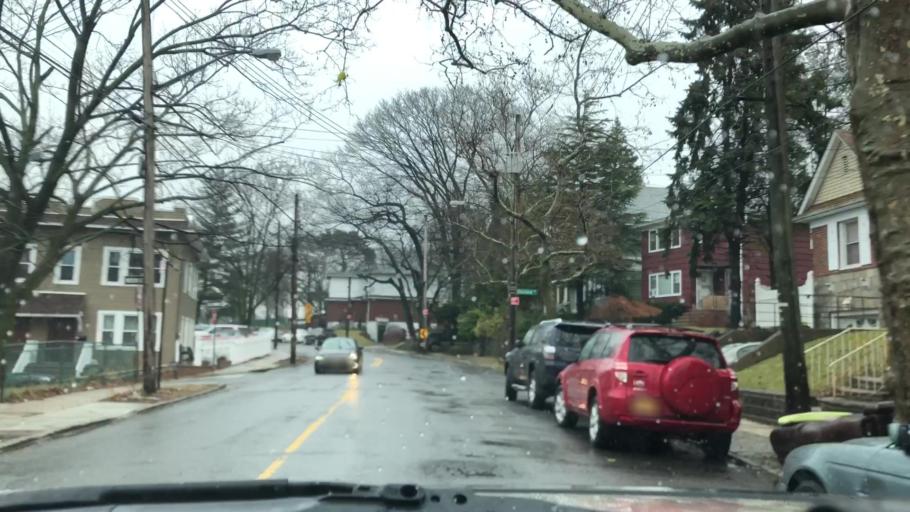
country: US
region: New Jersey
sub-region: Hudson County
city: Bayonne
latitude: 40.6333
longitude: -74.0940
